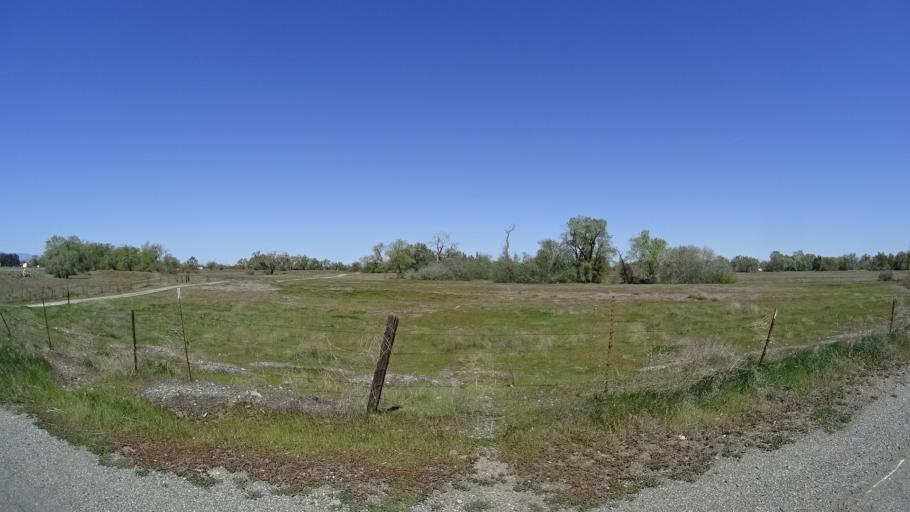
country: US
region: California
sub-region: Glenn County
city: Orland
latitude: 39.7842
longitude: -122.2516
